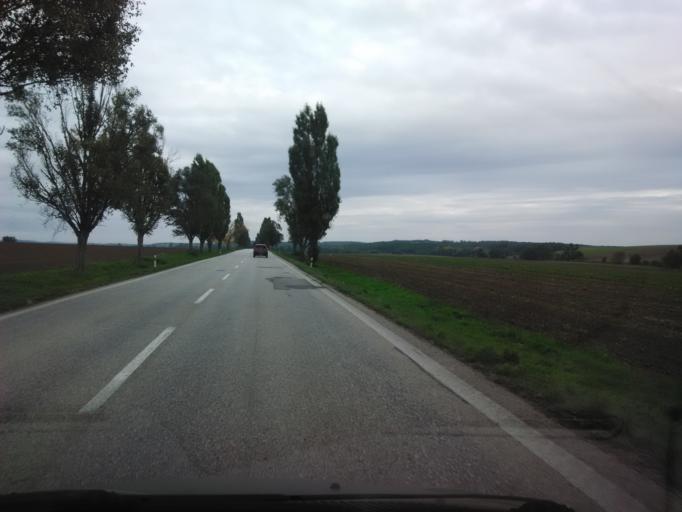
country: SK
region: Nitriansky
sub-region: Okres Nitra
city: Vrable
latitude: 48.2367
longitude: 18.3351
